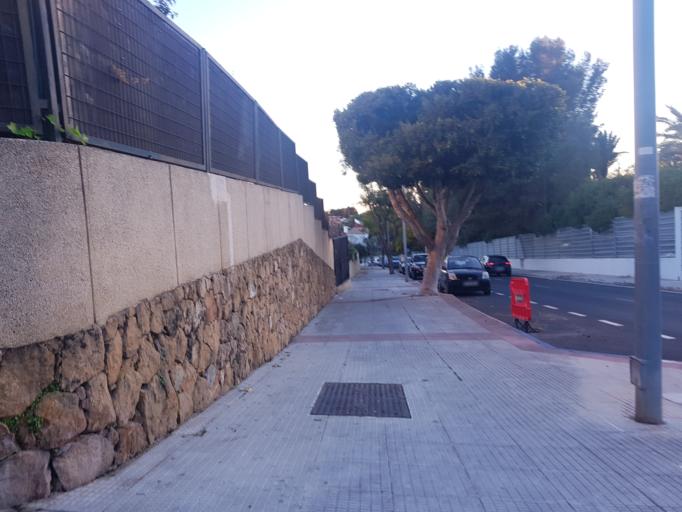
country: ES
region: Andalusia
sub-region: Provincia de Malaga
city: Marbella
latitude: 36.5247
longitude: -4.8913
